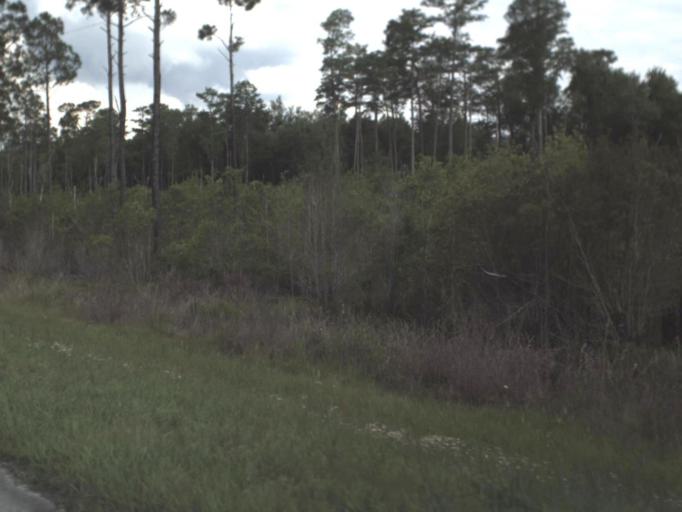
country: US
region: Florida
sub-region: Baker County
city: Macclenny
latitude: 30.5271
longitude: -82.3028
